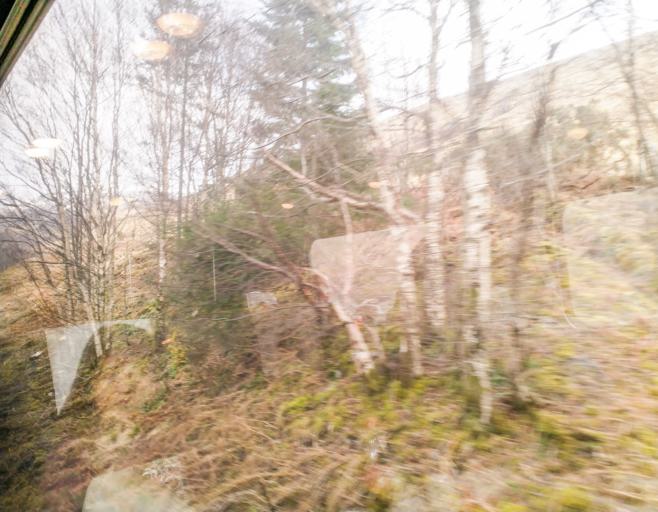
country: GB
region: Scotland
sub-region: Highland
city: Spean Bridge
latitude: 56.8040
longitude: -4.7194
